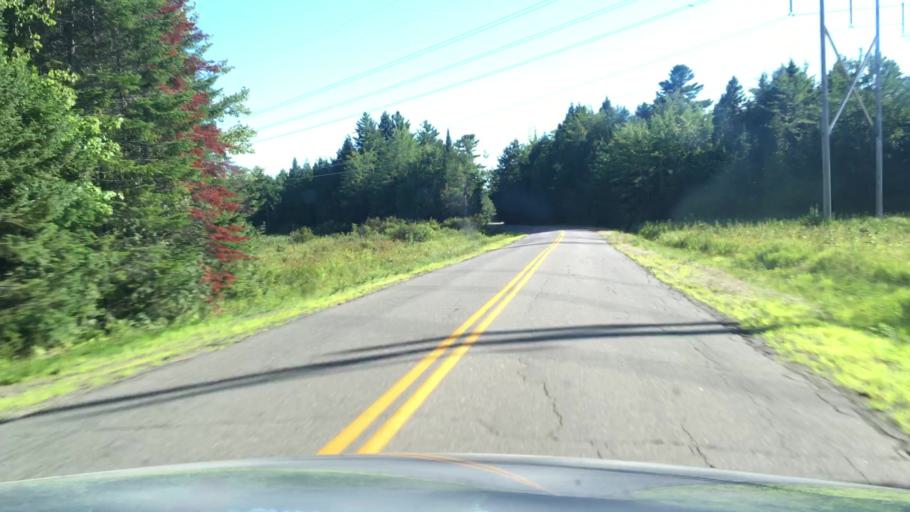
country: US
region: Maine
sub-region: Penobscot County
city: Enfield
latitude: 45.2100
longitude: -68.5906
